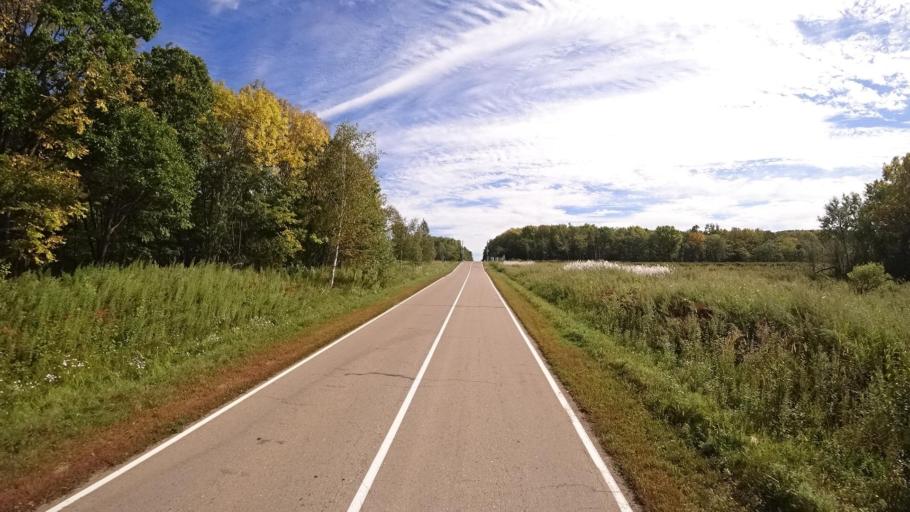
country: RU
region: Primorskiy
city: Yakovlevka
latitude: 44.4073
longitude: 133.5912
